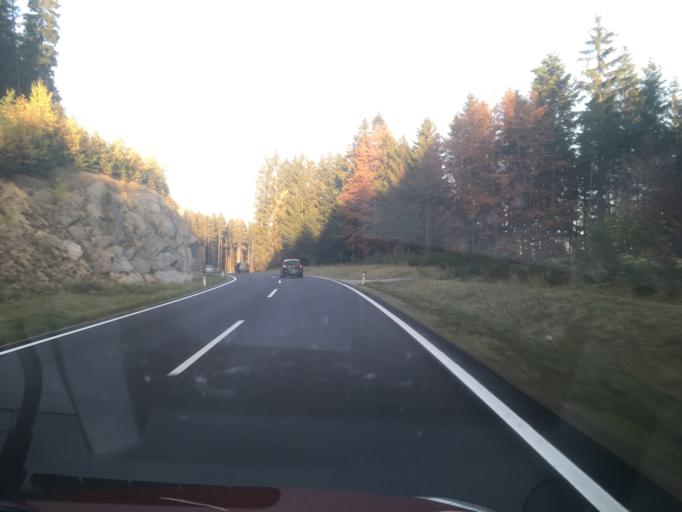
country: AT
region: Upper Austria
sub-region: Politischer Bezirk Freistadt
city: Freistadt
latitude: 48.5275
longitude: 14.5812
